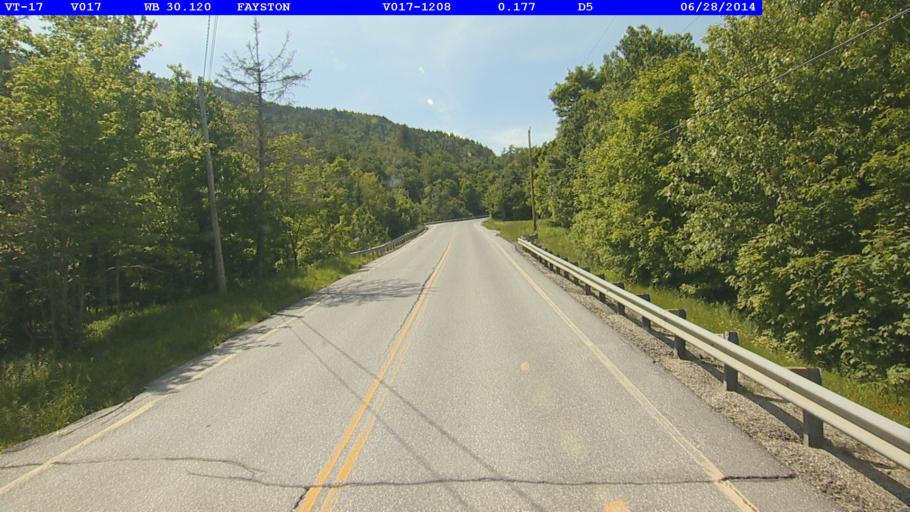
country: US
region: Vermont
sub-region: Addison County
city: Bristol
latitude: 44.2073
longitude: -72.9265
